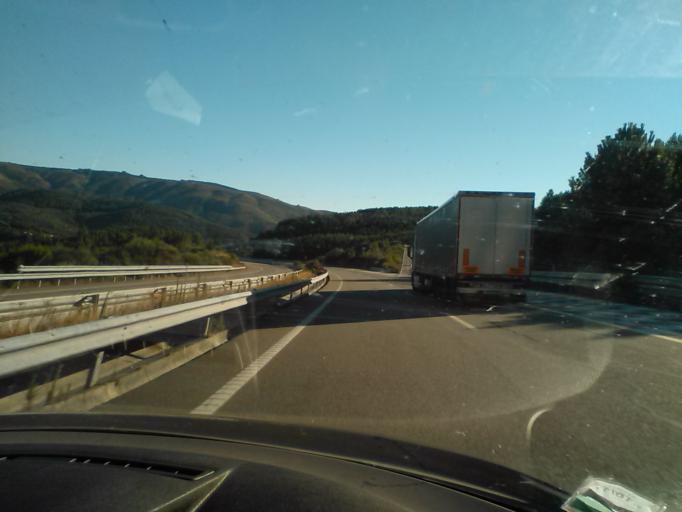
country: PT
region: Vila Real
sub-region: Ribeira de Pena
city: Ribeira de Pena
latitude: 41.4856
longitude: -7.8643
